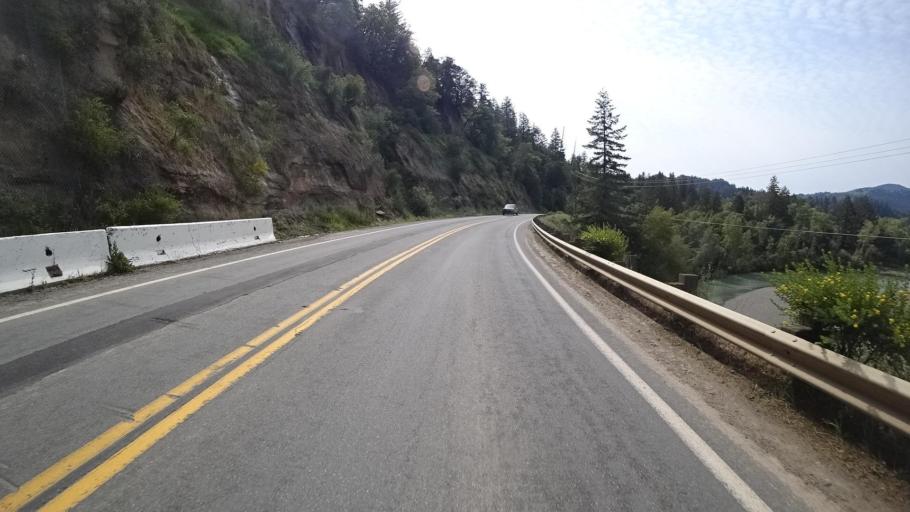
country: US
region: California
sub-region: Humboldt County
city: Redway
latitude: 40.1158
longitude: -123.7959
